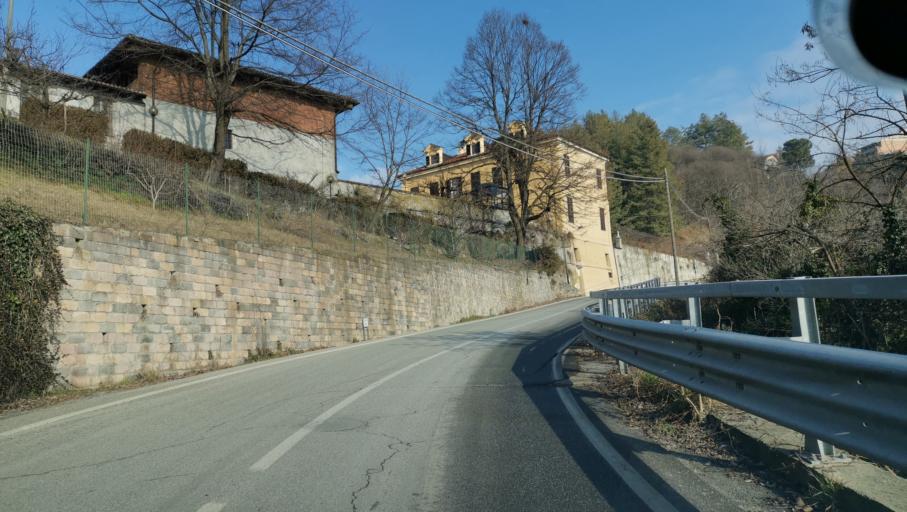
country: IT
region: Piedmont
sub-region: Provincia di Torino
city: Piana San Raffaele
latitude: 45.1501
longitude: 7.8604
